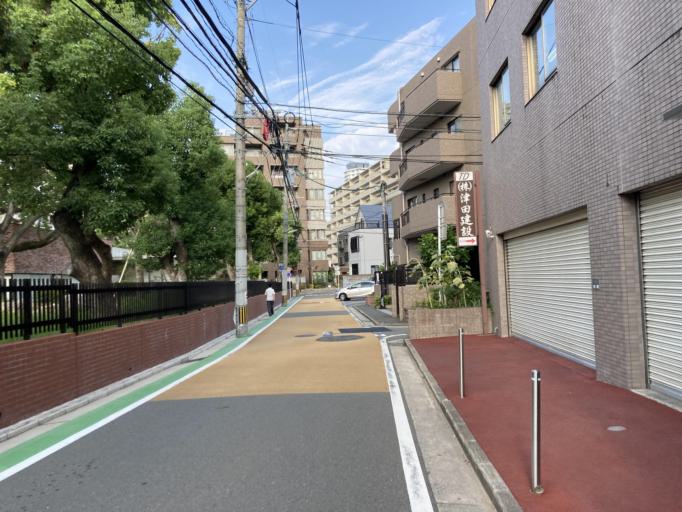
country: JP
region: Fukuoka
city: Fukuoka-shi
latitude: 33.5852
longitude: 130.3581
